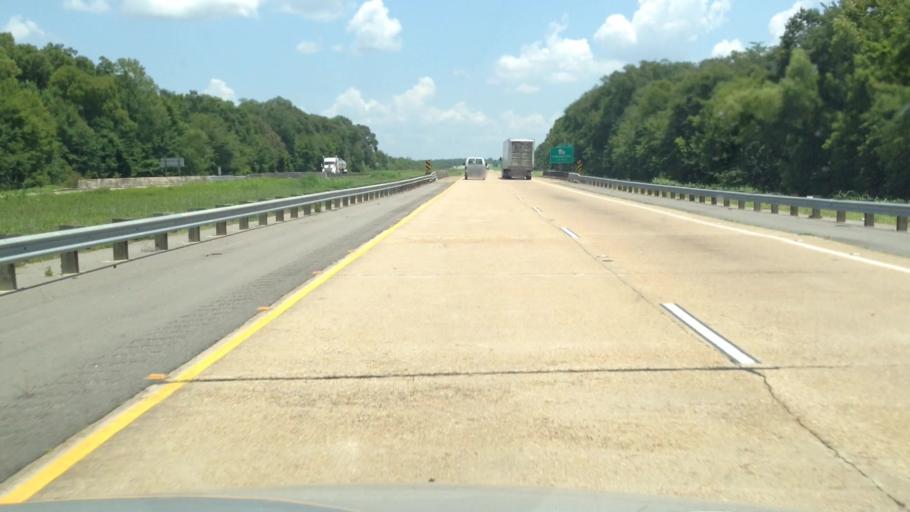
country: US
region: Louisiana
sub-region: Rapides Parish
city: Lecompte
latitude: 30.9937
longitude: -92.3236
